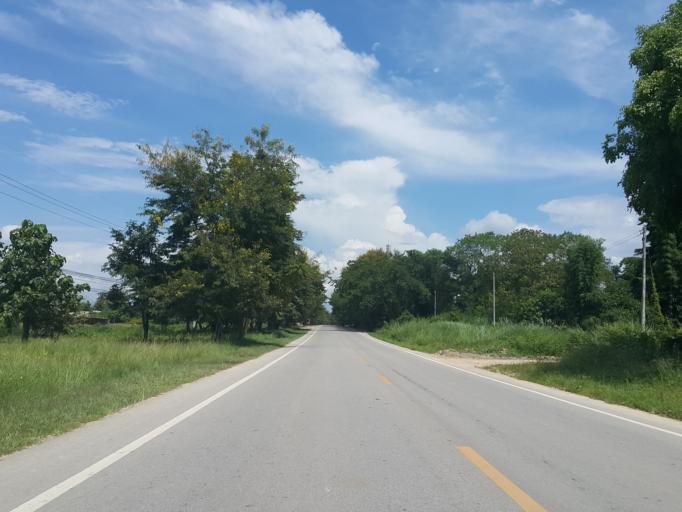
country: TH
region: Chiang Mai
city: Phrao
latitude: 19.2931
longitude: 99.1883
